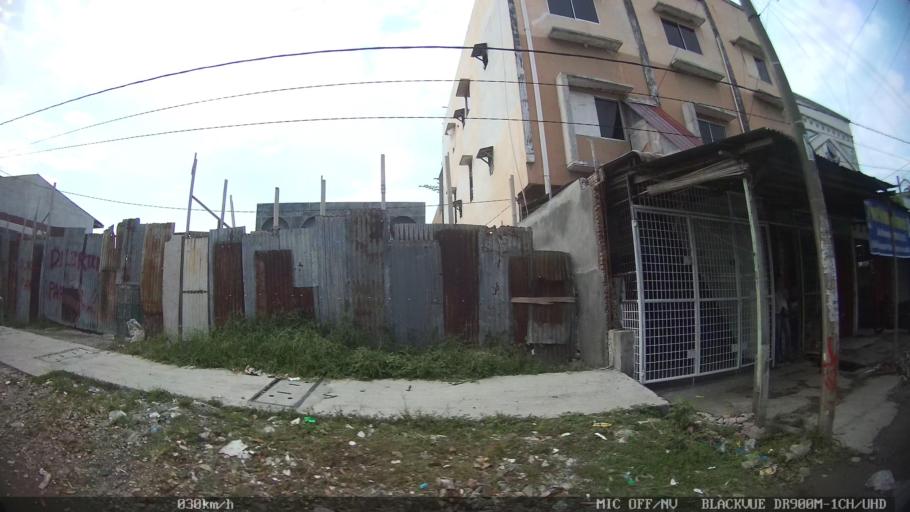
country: ID
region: North Sumatra
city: Medan
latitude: 3.6069
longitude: 98.7052
